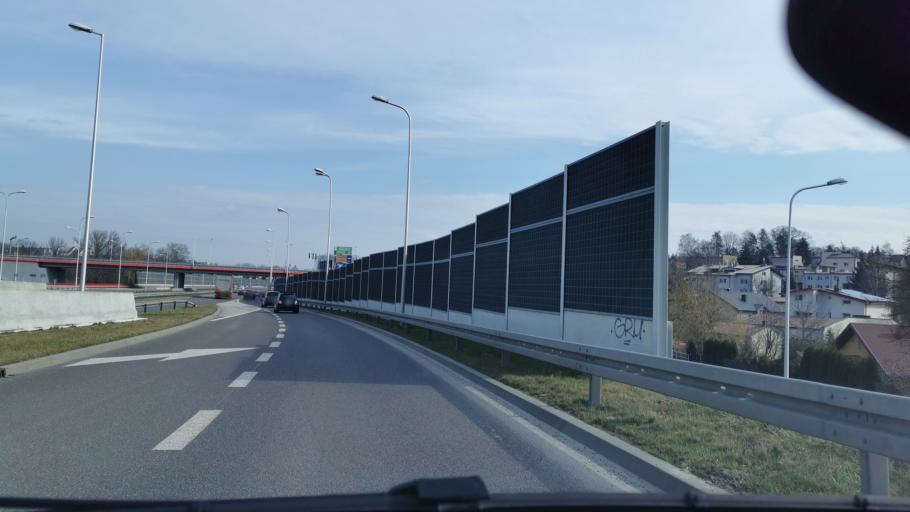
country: PL
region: Lublin Voivodeship
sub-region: Powiat lubelski
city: Lublin
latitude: 51.2571
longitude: 22.5106
